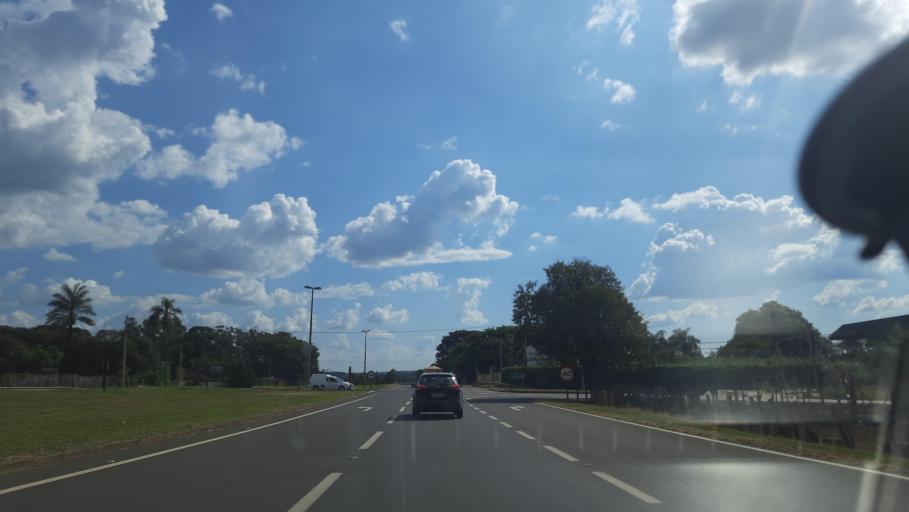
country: BR
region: Sao Paulo
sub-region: Casa Branca
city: Casa Branca
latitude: -21.7417
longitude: -46.9798
